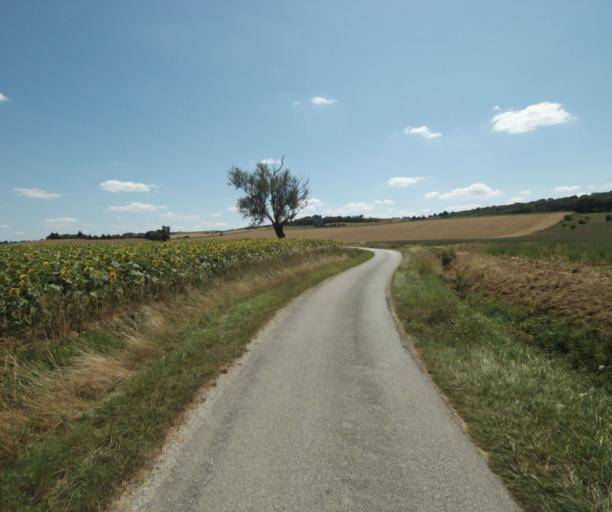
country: FR
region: Midi-Pyrenees
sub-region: Departement de la Haute-Garonne
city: Saint-Felix-Lauragais
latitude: 43.4835
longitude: 1.8762
